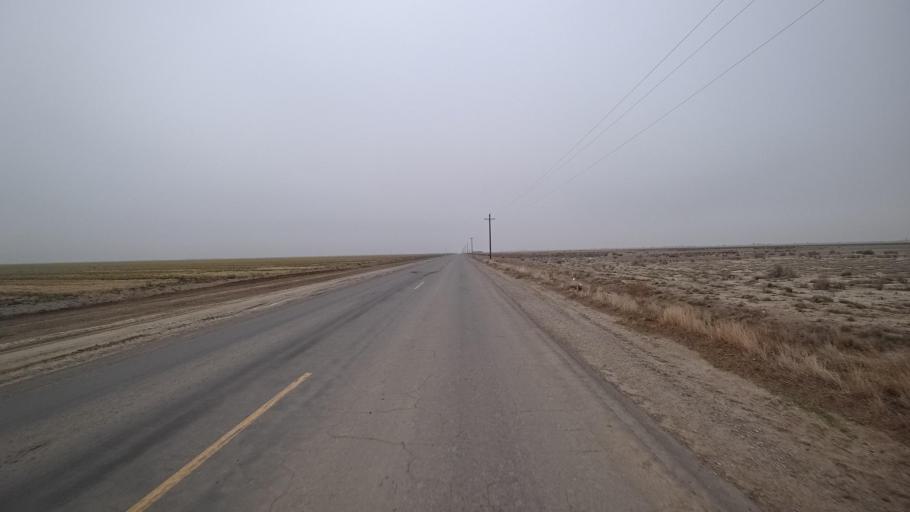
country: US
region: California
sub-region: Kern County
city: Rosedale
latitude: 35.2306
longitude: -119.2328
